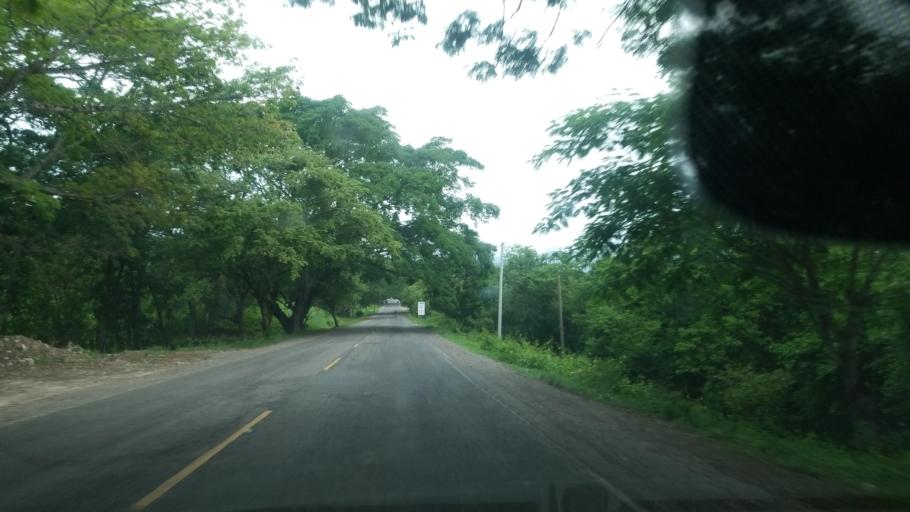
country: HN
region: Santa Barbara
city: San Vicente Centenario
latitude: 14.8858
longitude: -88.2487
